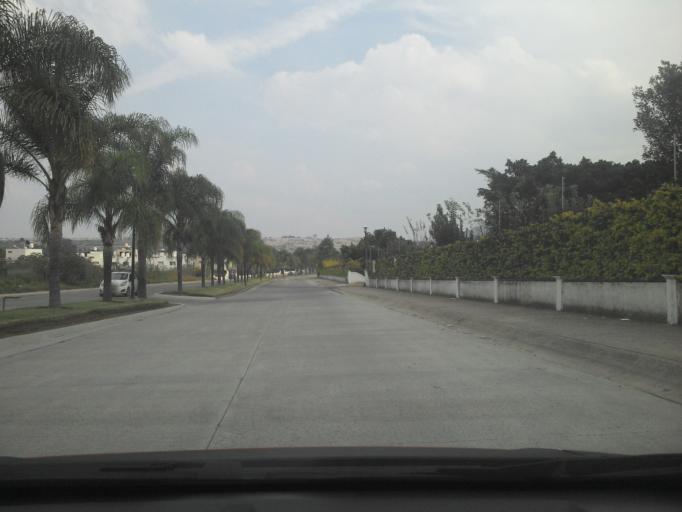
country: MX
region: Jalisco
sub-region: Tlajomulco de Zuniga
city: Lomas de San Agustin
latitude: 20.5308
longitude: -103.4726
